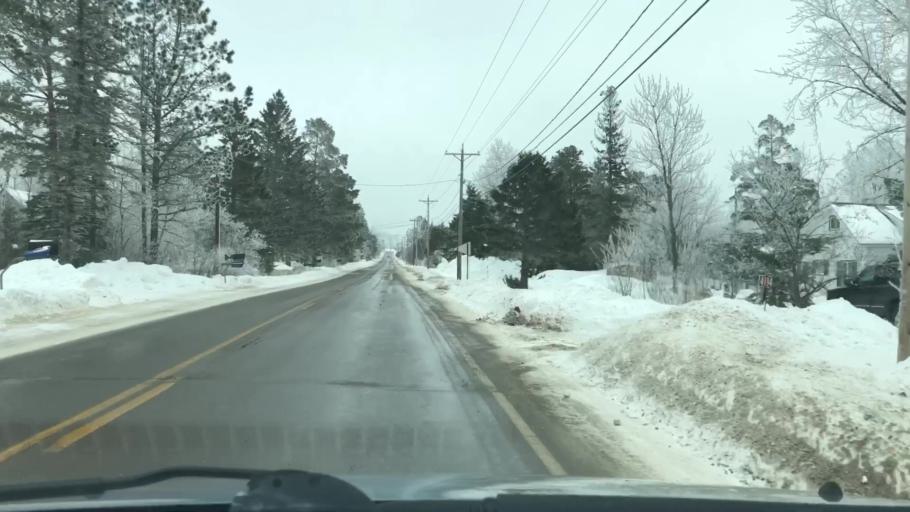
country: US
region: Minnesota
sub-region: Saint Louis County
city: Arnold
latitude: 46.8595
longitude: -92.1209
